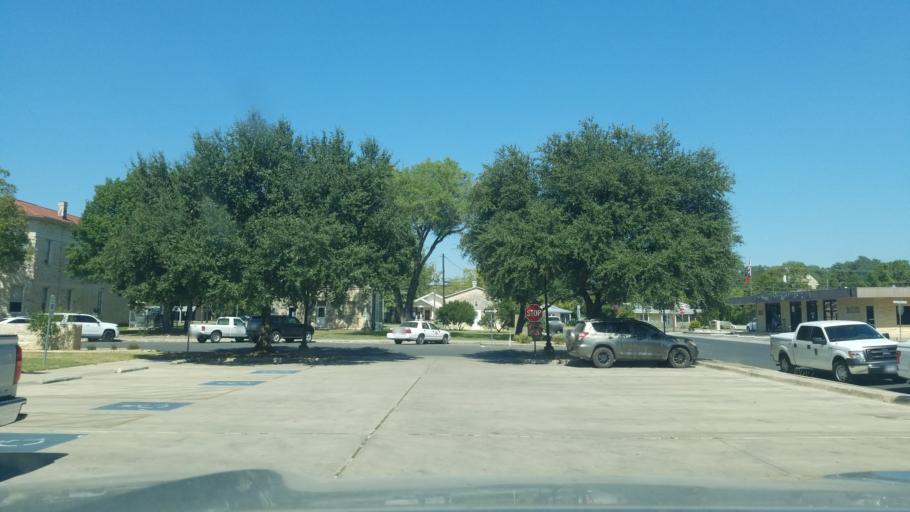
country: US
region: Texas
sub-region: Kendall County
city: Boerne
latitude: 29.7942
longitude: -98.7302
